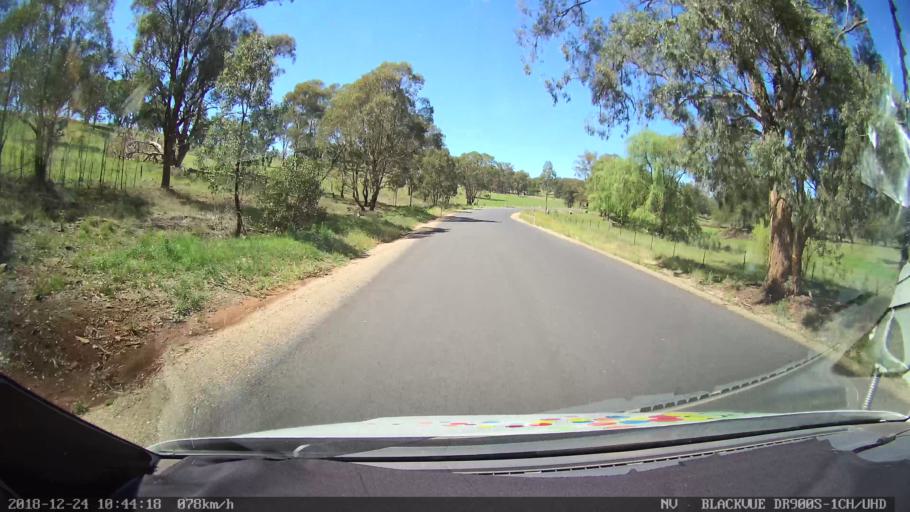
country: AU
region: New South Wales
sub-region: Upper Hunter Shire
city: Merriwa
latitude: -31.8915
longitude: 150.4440
